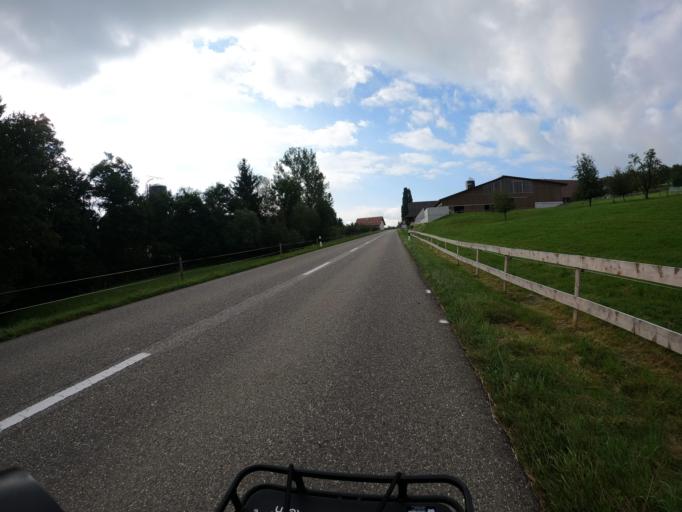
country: CH
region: Aargau
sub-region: Bezirk Muri
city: Buttwil
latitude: 47.2511
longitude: 8.3210
